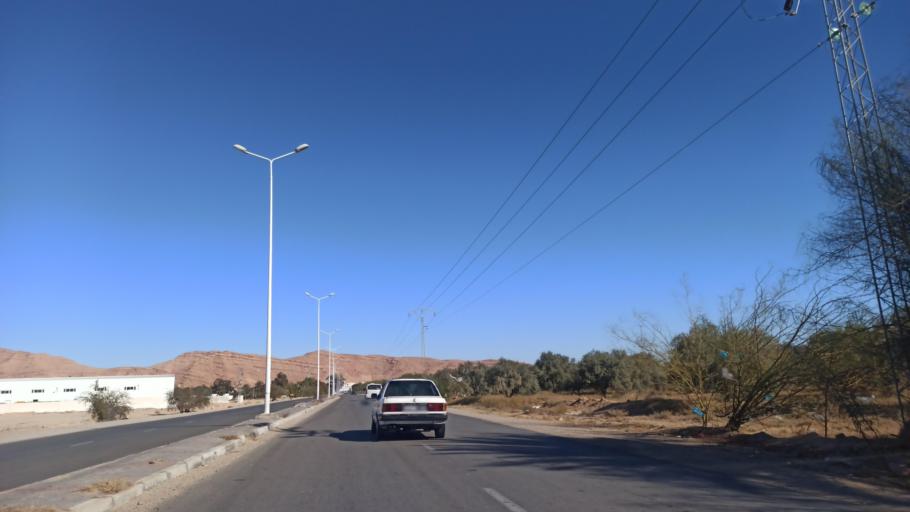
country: TN
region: Gafsa
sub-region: Gafsa Municipality
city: Gafsa
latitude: 34.4148
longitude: 8.7408
